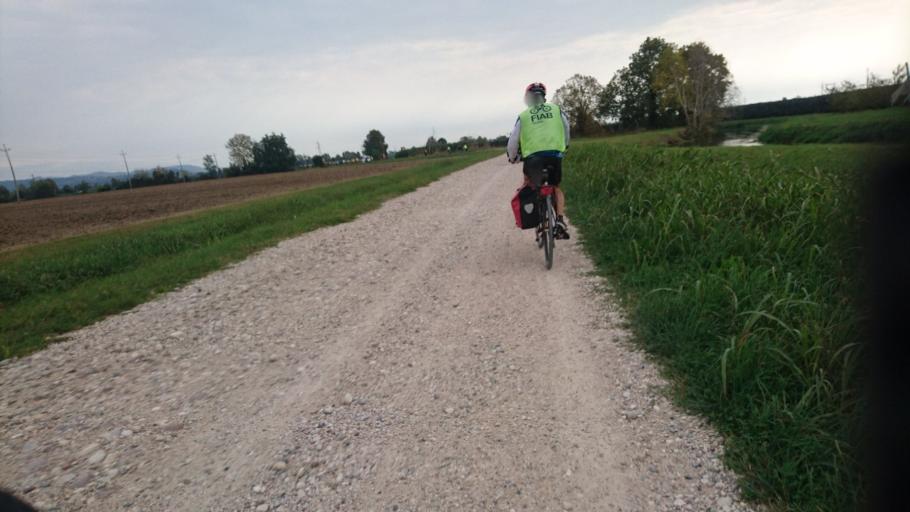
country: IT
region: Veneto
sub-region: Provincia di Verona
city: Zevio
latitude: 45.3983
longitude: 11.1181
